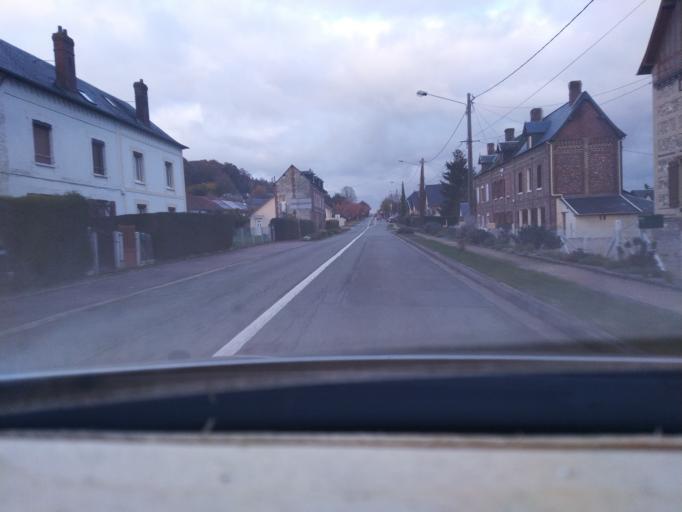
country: FR
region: Haute-Normandie
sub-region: Departement de la Seine-Maritime
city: Duclair
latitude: 49.4722
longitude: 0.8612
